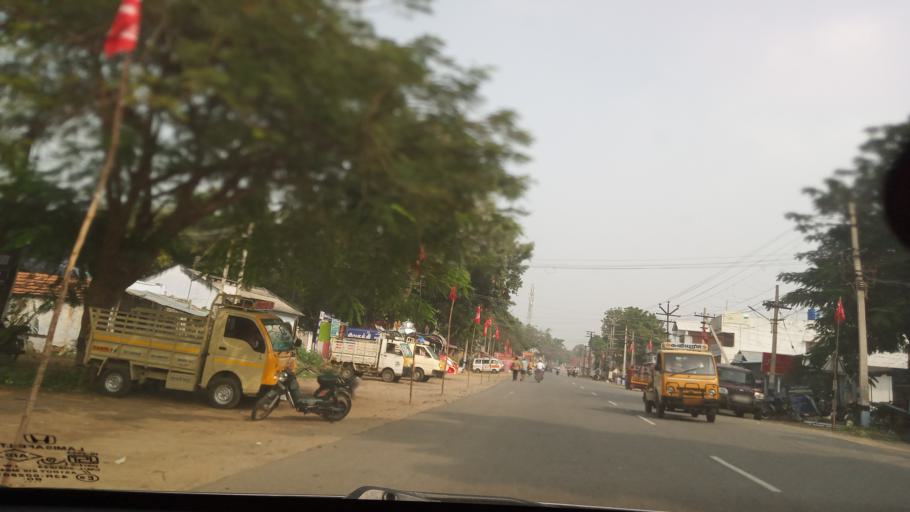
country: IN
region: Tamil Nadu
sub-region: Erode
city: Punjai Puliyampatti
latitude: 11.3553
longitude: 77.1695
